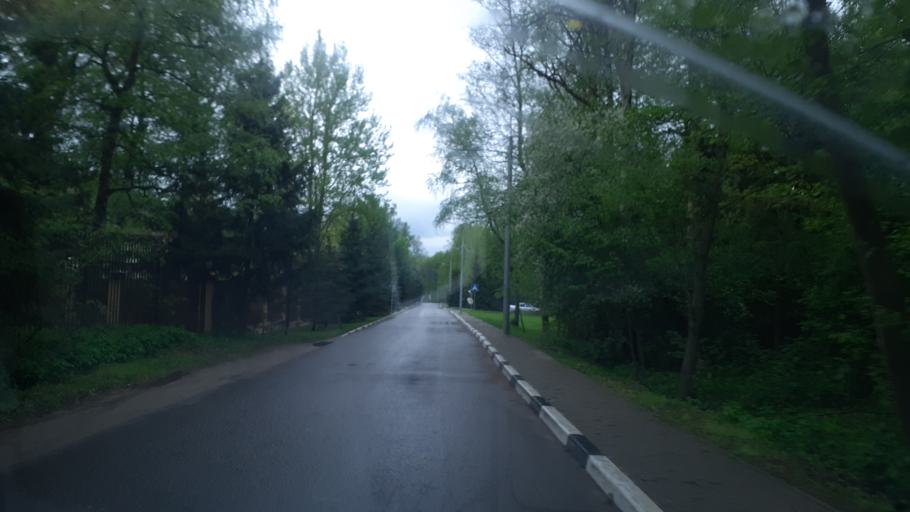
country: RU
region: Moskovskaya
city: Gorki Vtoryye
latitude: 55.7085
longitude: 37.2047
